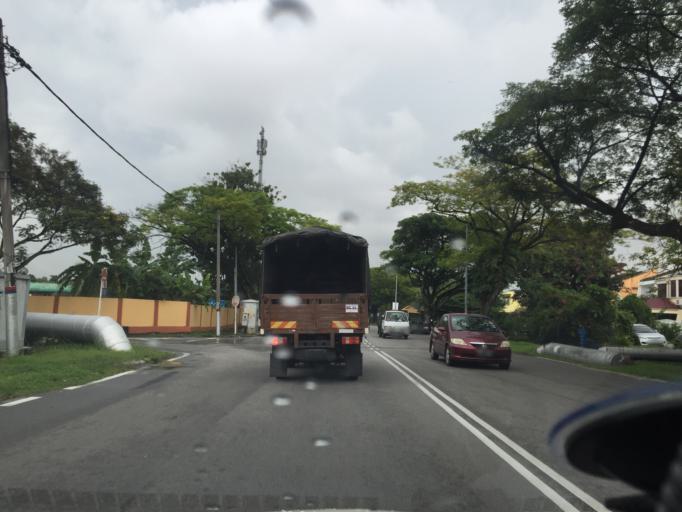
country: MY
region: Selangor
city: Klang
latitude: 3.0098
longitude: 101.4470
